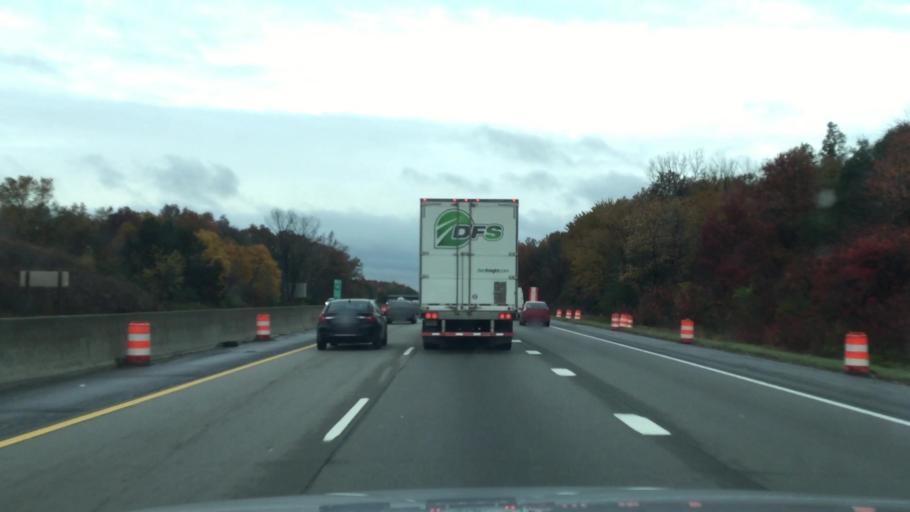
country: US
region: Michigan
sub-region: Washtenaw County
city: Ypsilanti
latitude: 42.2248
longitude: -83.6729
